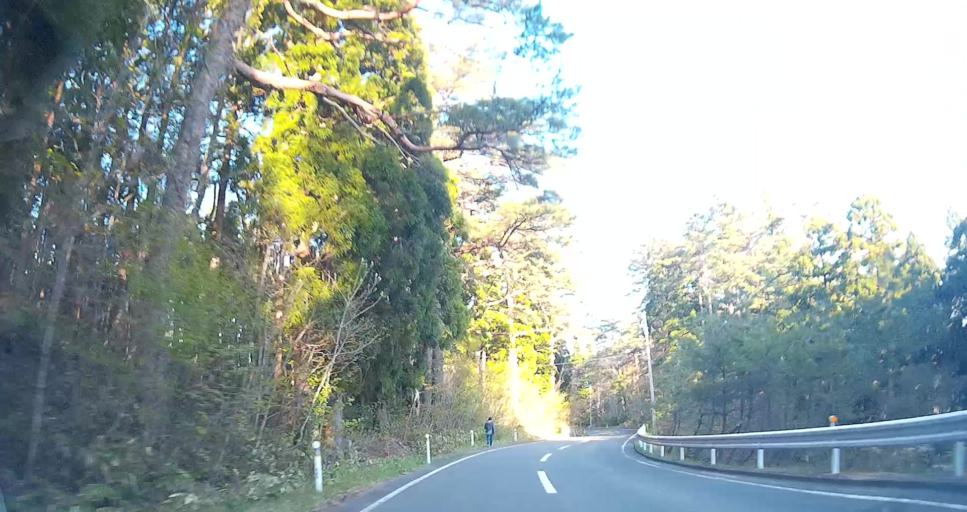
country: JP
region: Aomori
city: Mutsu
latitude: 41.3196
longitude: 141.1427
